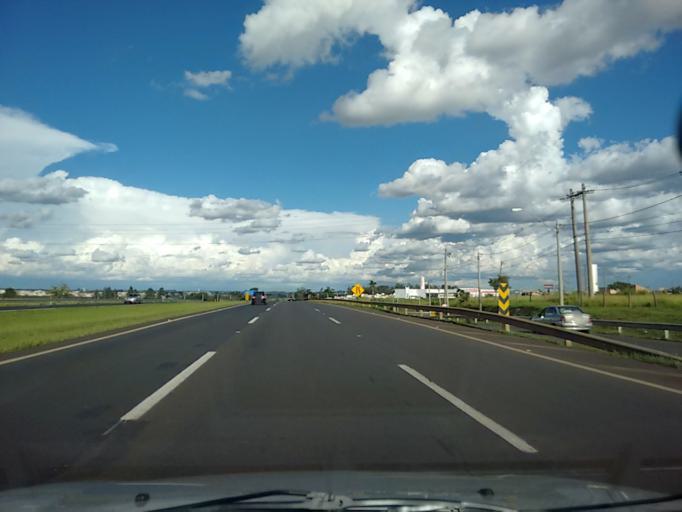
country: BR
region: Sao Paulo
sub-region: Sao Carlos
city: Sao Carlos
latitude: -21.9759
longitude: -47.9343
